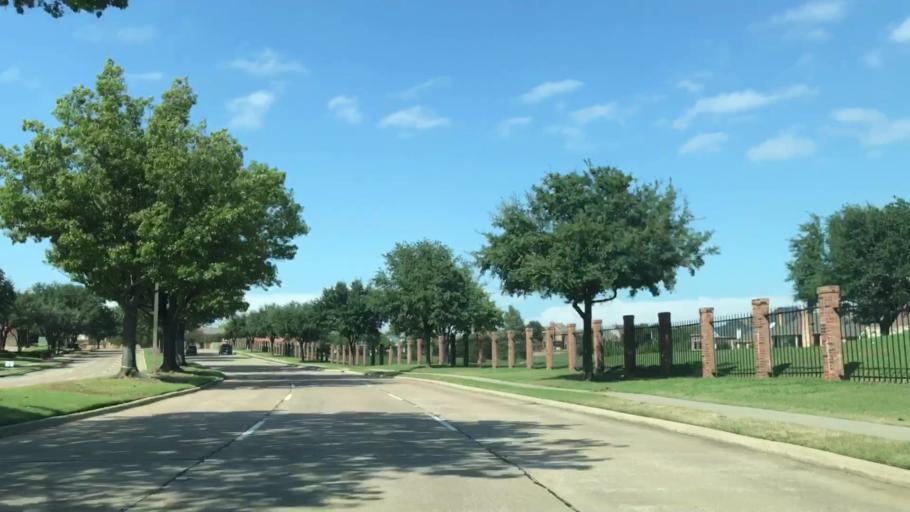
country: US
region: Texas
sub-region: Dallas County
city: Coppell
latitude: 32.9087
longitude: -96.9818
